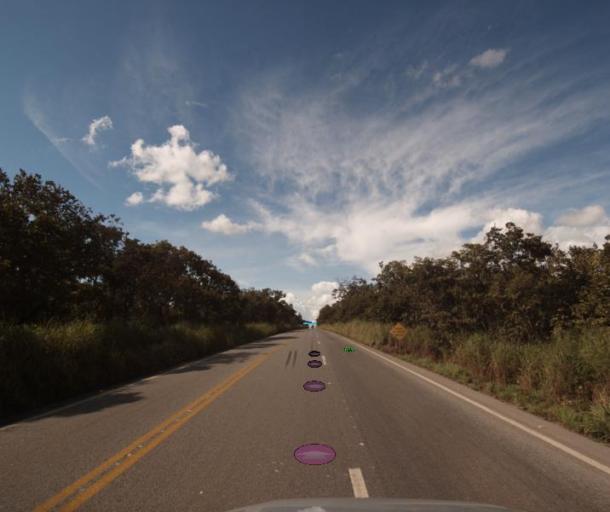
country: BR
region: Goias
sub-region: Porangatu
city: Porangatu
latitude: -13.0676
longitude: -49.1844
